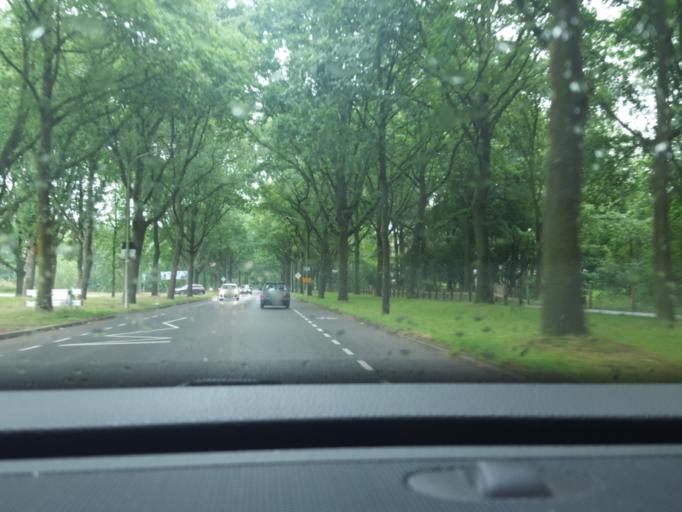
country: NL
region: Gelderland
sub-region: Gemeente Doetinchem
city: Doetinchem
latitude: 51.9742
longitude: 6.3032
